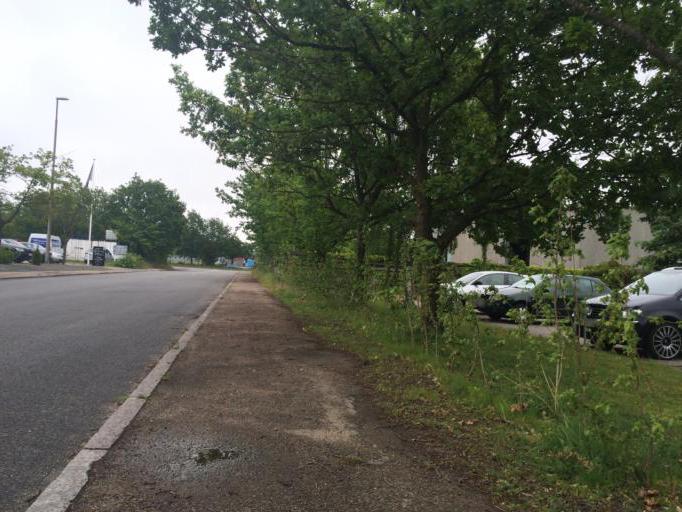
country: DK
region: Capital Region
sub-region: Hvidovre Kommune
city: Hvidovre
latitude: 55.6123
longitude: 12.4735
